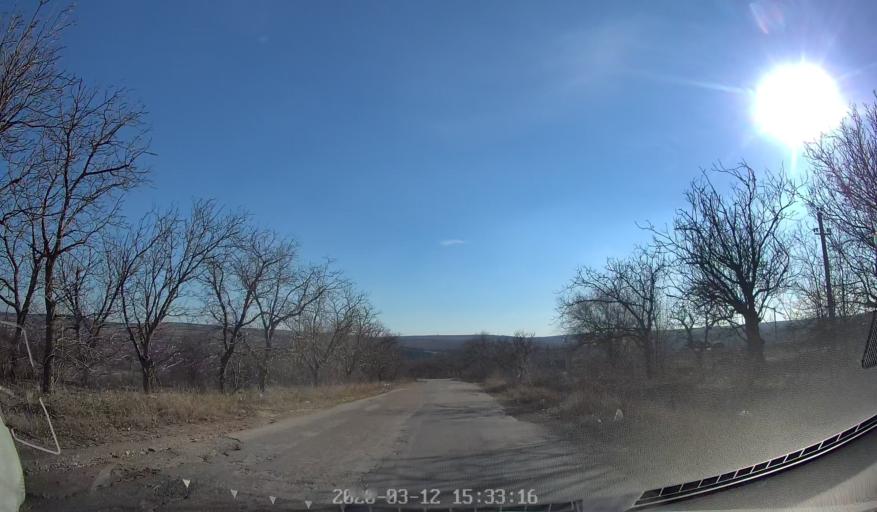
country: MD
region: Chisinau
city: Ciorescu
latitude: 47.1447
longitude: 28.9378
